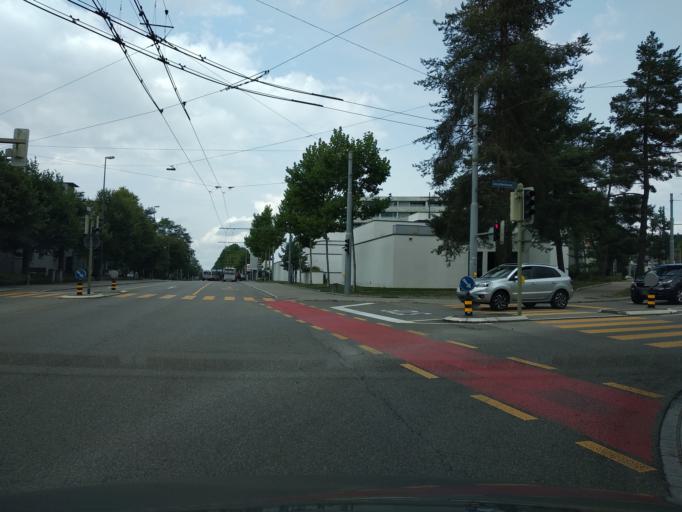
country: CH
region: Zurich
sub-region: Bezirk Winterthur
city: Veltheim
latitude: 47.5166
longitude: 8.7202
